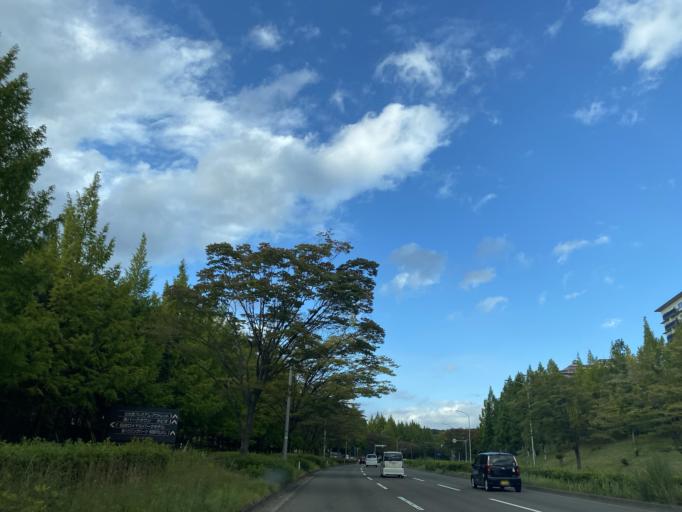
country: JP
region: Miyagi
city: Tomiya
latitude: 38.3388
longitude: 140.8388
